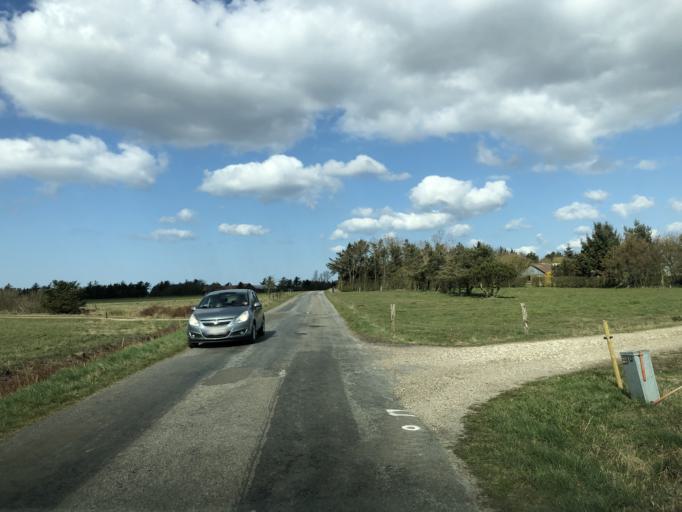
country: DK
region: Central Jutland
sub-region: Holstebro Kommune
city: Ulfborg
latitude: 56.3749
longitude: 8.2122
